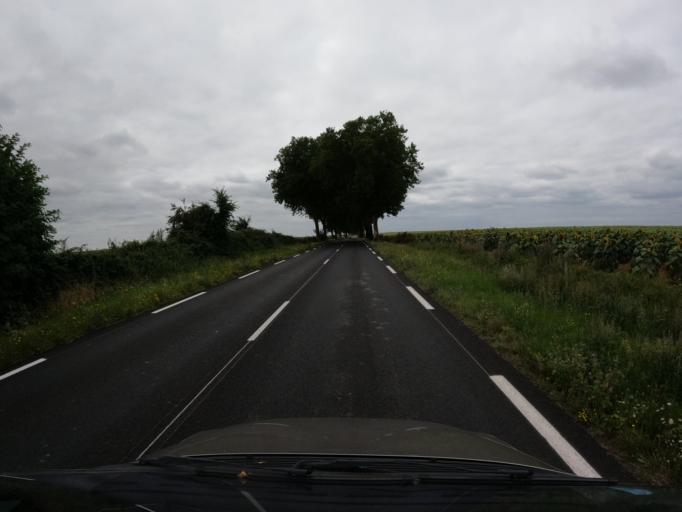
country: FR
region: Pays de la Loire
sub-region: Departement de la Vendee
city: Saint-Martin-sous-Mouzeuil
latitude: 46.5120
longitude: -0.9609
